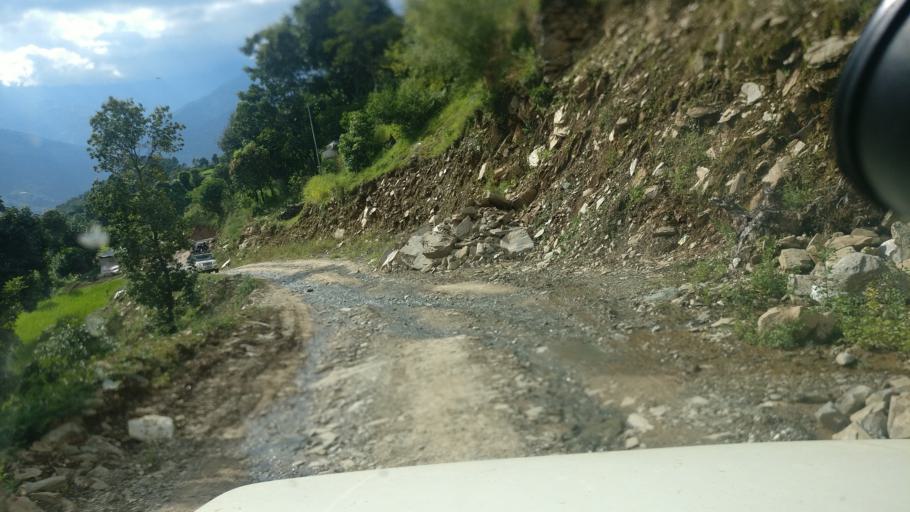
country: NP
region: Western Region
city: Baglung
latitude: 28.2643
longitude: 83.6422
